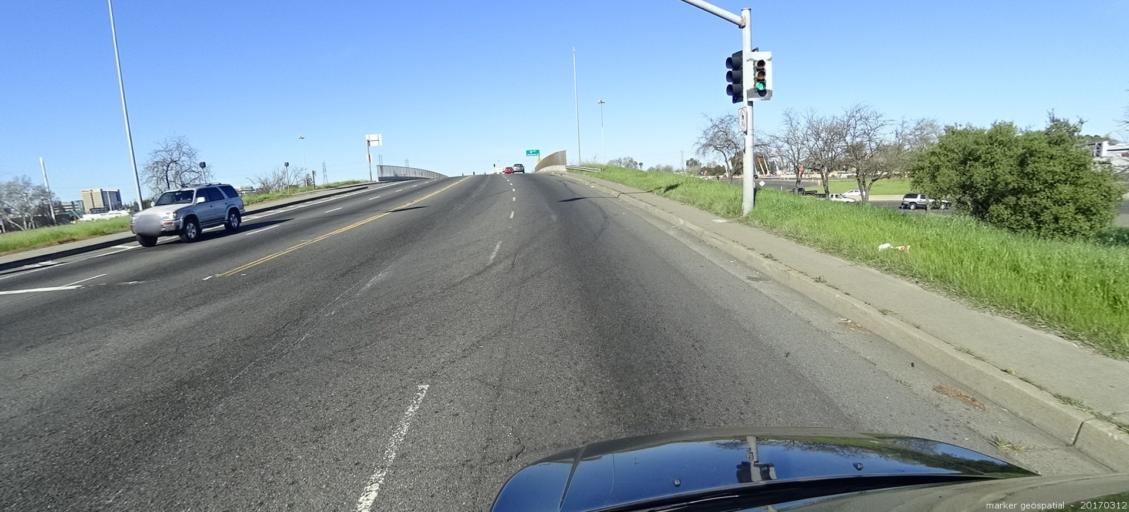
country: US
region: California
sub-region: Sacramento County
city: Arden-Arcade
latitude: 38.6112
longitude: -121.4252
